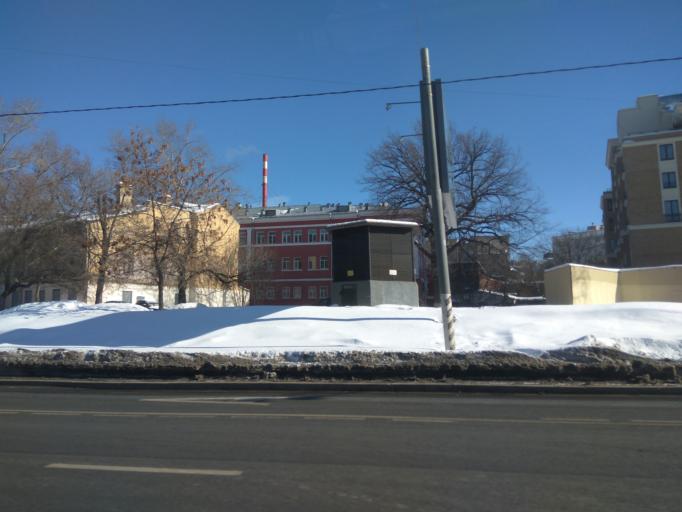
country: RU
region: Moscow
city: Taganskiy
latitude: 55.7334
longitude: 37.6585
